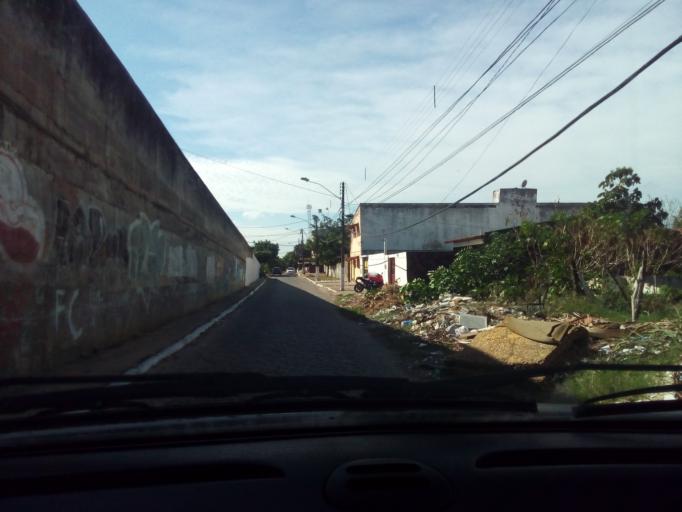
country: BR
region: Rio Grande do Norte
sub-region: Parnamirim
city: Parnamirim
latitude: -5.8854
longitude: -35.2039
